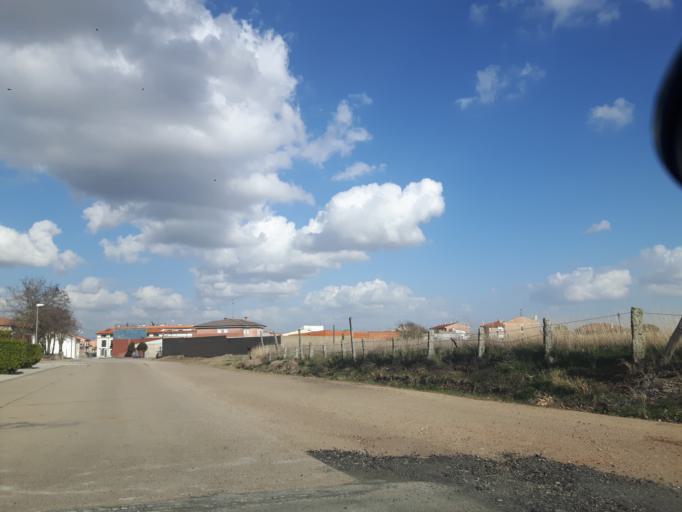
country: ES
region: Castille and Leon
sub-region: Provincia de Salamanca
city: Moriscos
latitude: 41.0066
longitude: -5.5856
